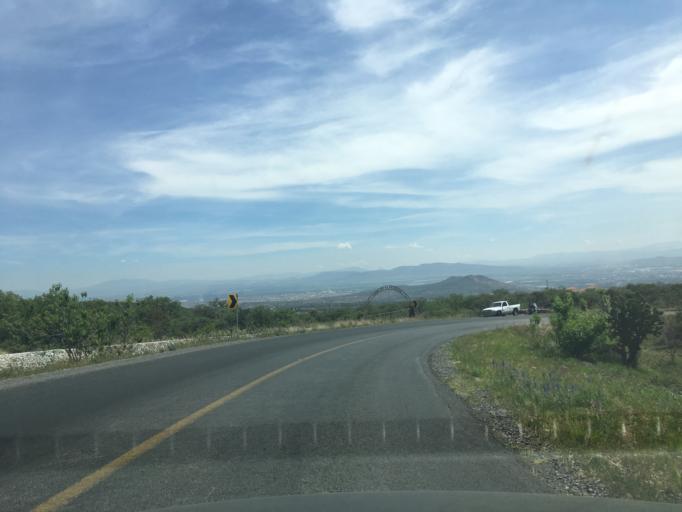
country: MX
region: Queretaro
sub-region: San Juan del Rio
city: El Jazmin
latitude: 20.3320
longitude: -100.0422
